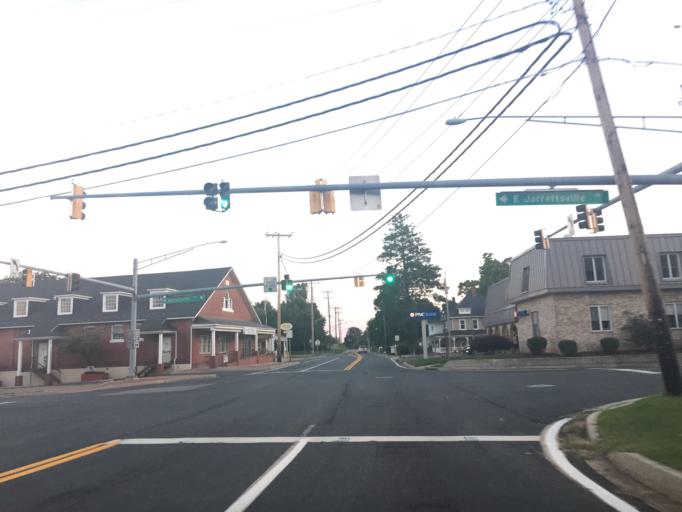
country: US
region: Maryland
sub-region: Harford County
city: Bel Air North
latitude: 39.5853
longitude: -76.3877
